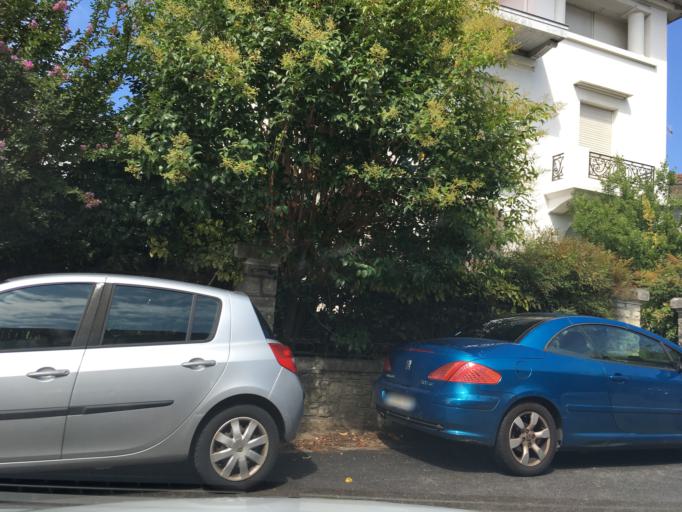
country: FR
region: Aquitaine
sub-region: Departement des Pyrenees-Atlantiques
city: Bayonne
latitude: 43.4888
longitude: -1.4833
